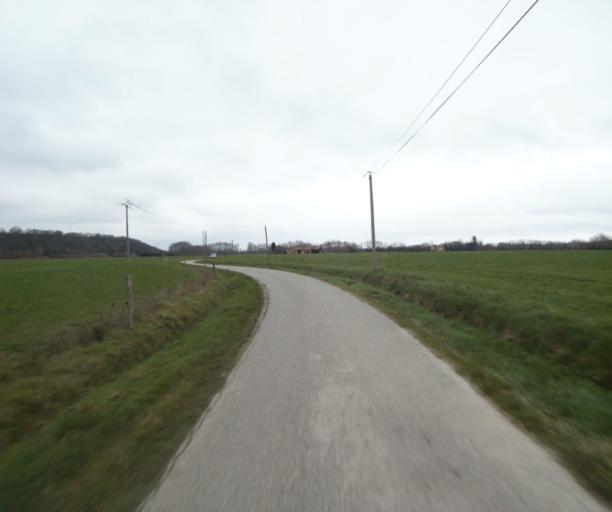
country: FR
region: Midi-Pyrenees
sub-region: Departement de l'Ariege
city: Saverdun
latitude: 43.2136
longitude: 1.5940
